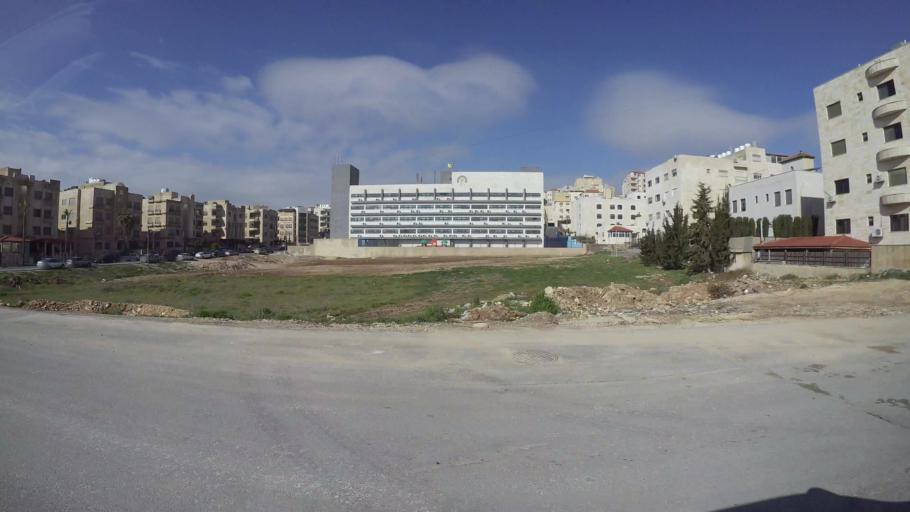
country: JO
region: Amman
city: Al Jubayhah
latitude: 32.0018
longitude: 35.8468
